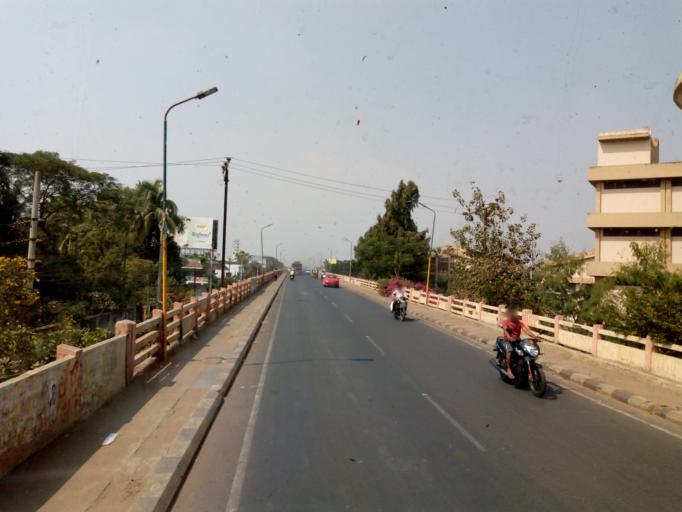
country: IN
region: Andhra Pradesh
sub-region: West Godavari
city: Eluru
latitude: 16.7085
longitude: 81.0997
